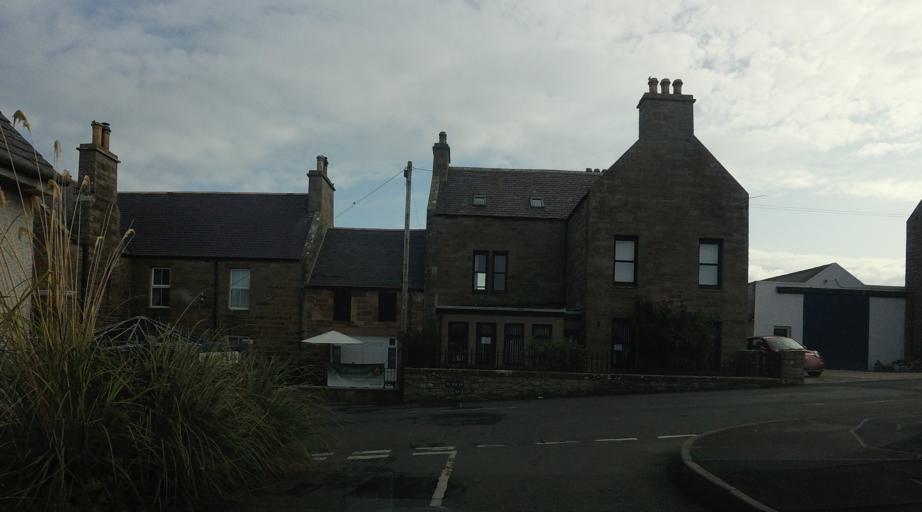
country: GB
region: Scotland
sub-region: Orkney Islands
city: Orkney
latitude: 58.8251
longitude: -2.9564
